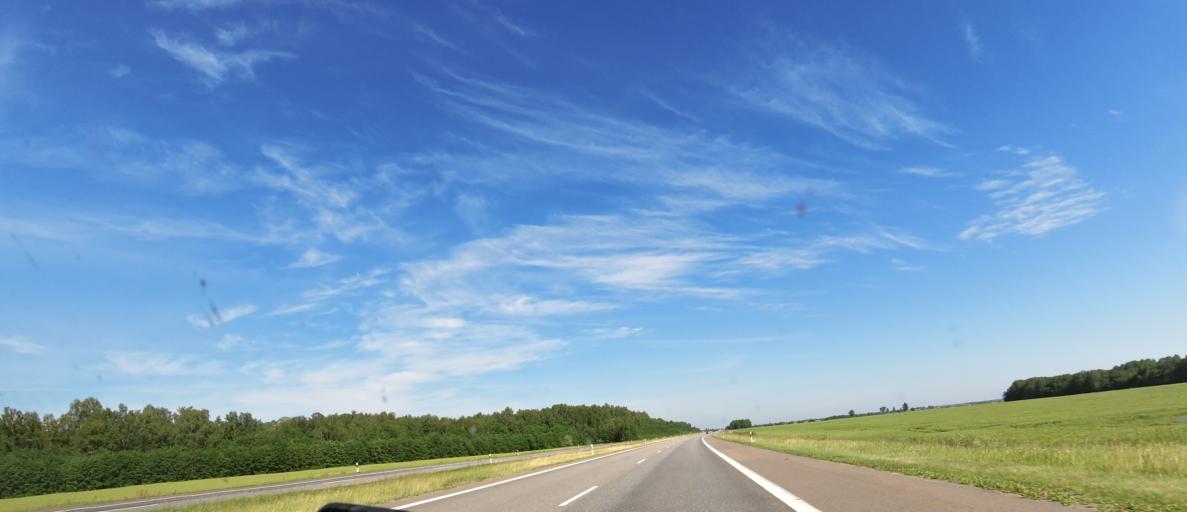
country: LT
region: Vilnius County
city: Ukmerge
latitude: 55.3331
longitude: 24.7637
